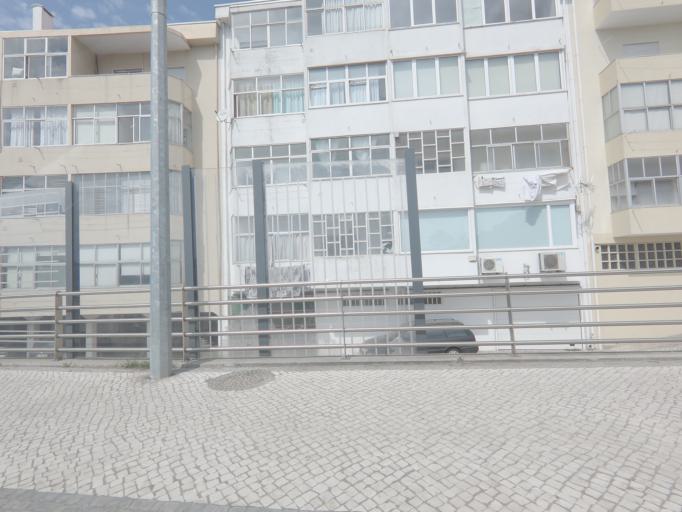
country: PT
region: Leiria
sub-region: Leiria
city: Leiria
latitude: 39.7454
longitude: -8.8173
